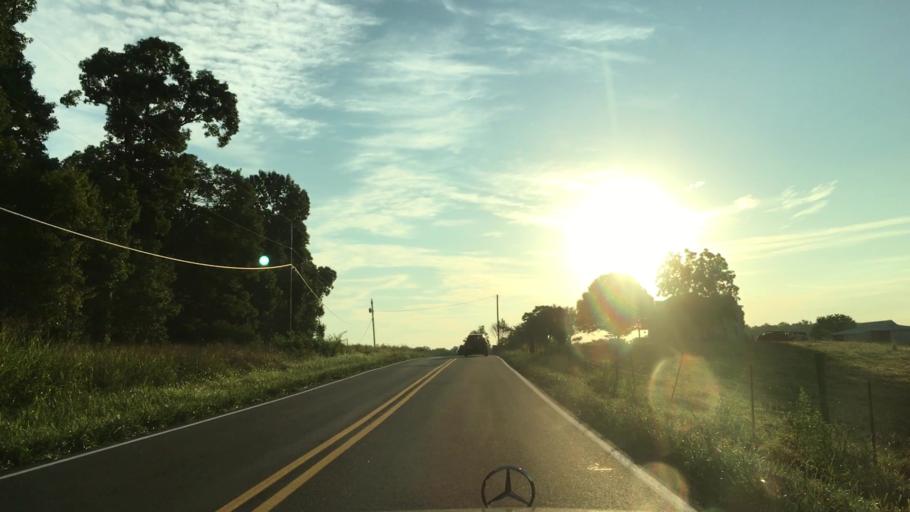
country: US
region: Virginia
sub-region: Campbell County
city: Timberlake
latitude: 37.2879
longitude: -79.2403
